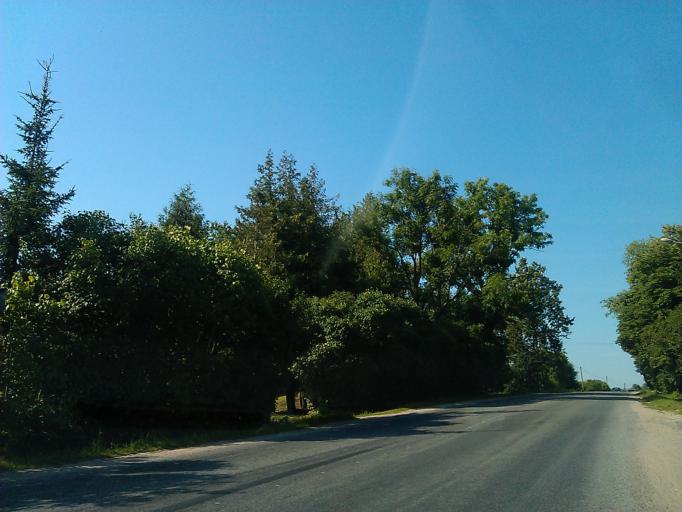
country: LV
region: Aizpute
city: Aizpute
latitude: 56.7209
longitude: 21.5937
